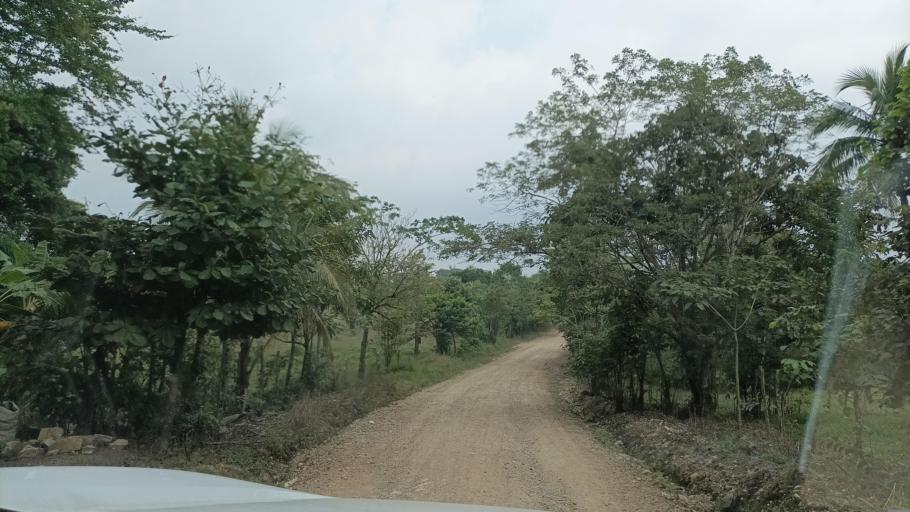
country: MX
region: Veracruz
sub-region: Moloacan
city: Cuichapa
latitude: 17.5795
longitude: -94.2256
